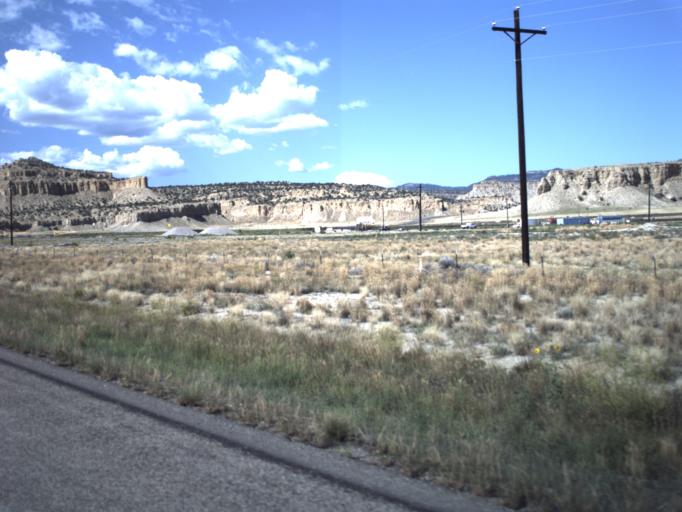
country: US
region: Utah
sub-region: Emery County
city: Ferron
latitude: 38.8537
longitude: -111.3062
